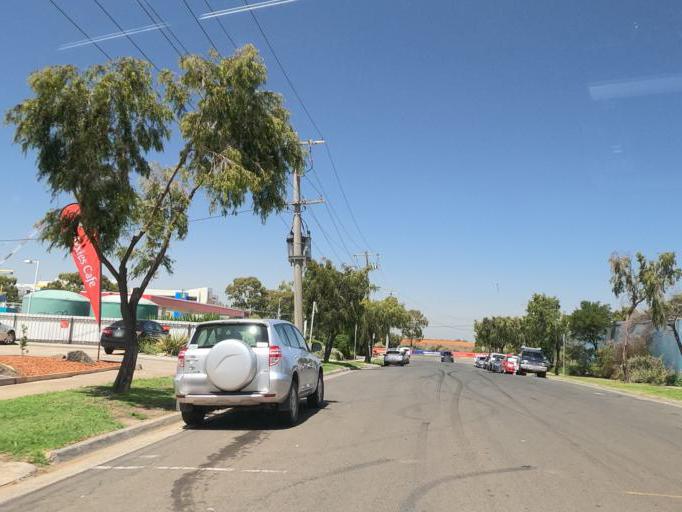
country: AU
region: Victoria
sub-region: Whittlesea
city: Lalor
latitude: -37.6494
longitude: 145.0118
